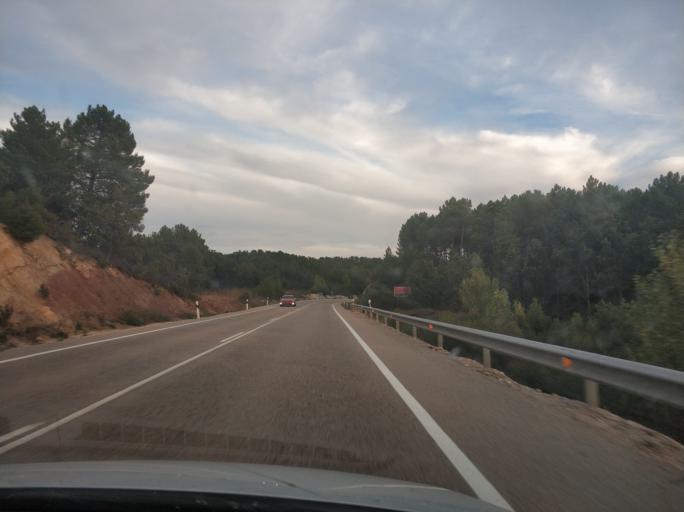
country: ES
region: Castille and Leon
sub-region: Provincia de Burgos
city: Pinilla de los Barruecos
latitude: 41.9139
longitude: -3.2772
